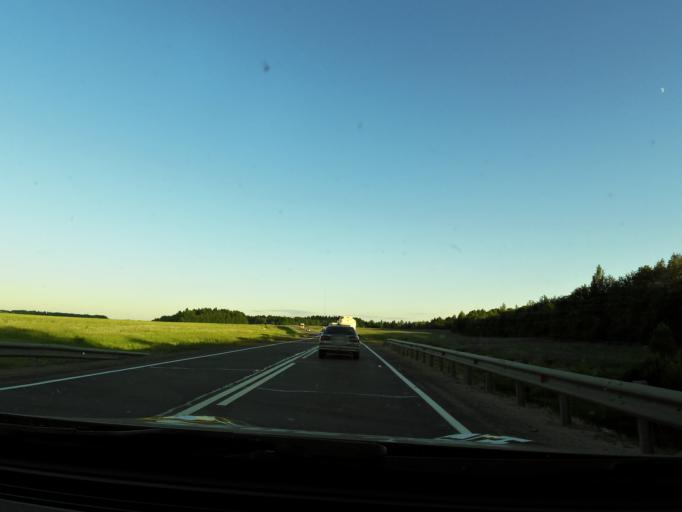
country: RU
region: Vologda
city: Gryazovets
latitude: 58.8415
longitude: 40.2048
